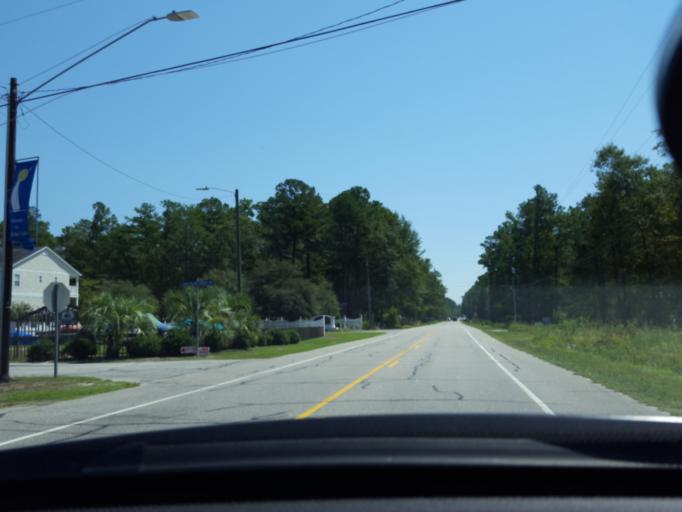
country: US
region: North Carolina
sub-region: Bladen County
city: Elizabethtown
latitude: 34.6317
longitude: -78.5036
